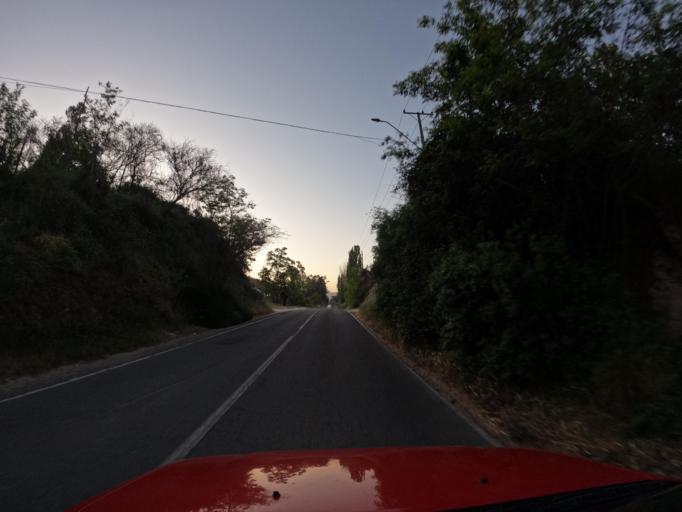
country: CL
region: O'Higgins
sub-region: Provincia de Cachapoal
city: San Vicente
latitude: -34.1581
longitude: -71.4159
